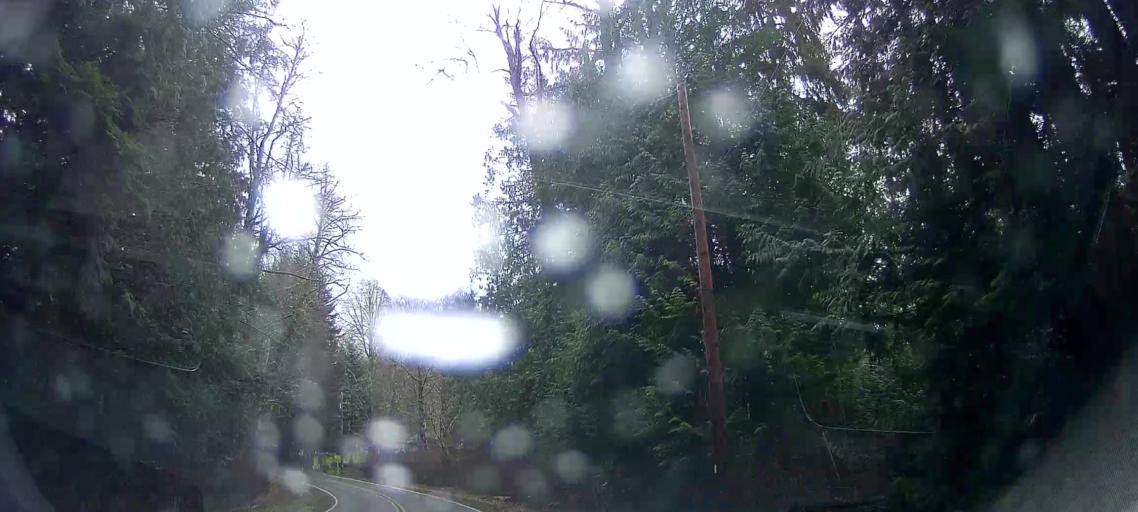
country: US
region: Washington
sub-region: Skagit County
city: Clear Lake
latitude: 48.4686
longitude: -122.1765
